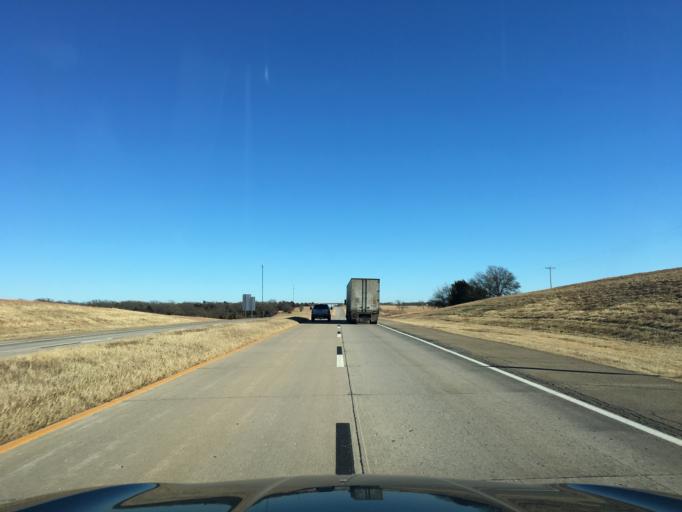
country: US
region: Oklahoma
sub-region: Pawnee County
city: Pawnee
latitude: 36.2246
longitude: -96.7619
